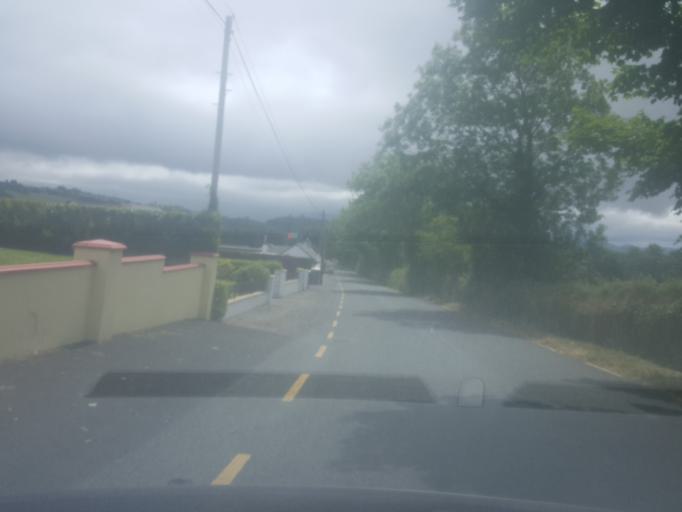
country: IE
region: Munster
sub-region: Ciarrai
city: Cill Airne
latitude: 52.0887
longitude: -9.4817
